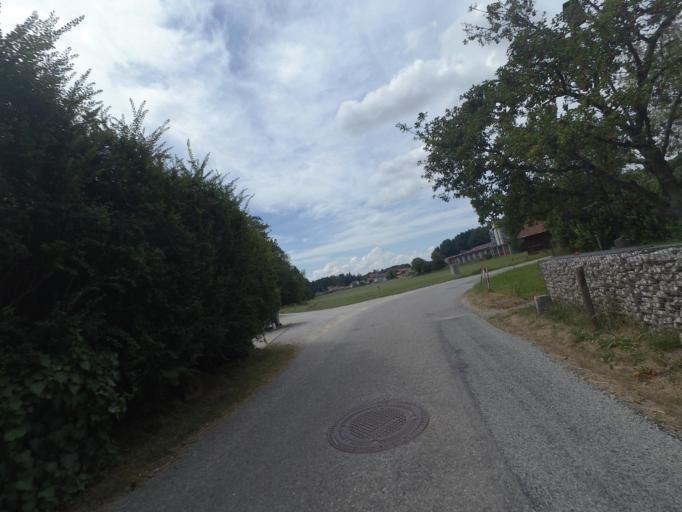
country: AT
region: Salzburg
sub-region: Politischer Bezirk Salzburg-Umgebung
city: Elixhausen
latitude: 47.8862
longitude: 13.0824
